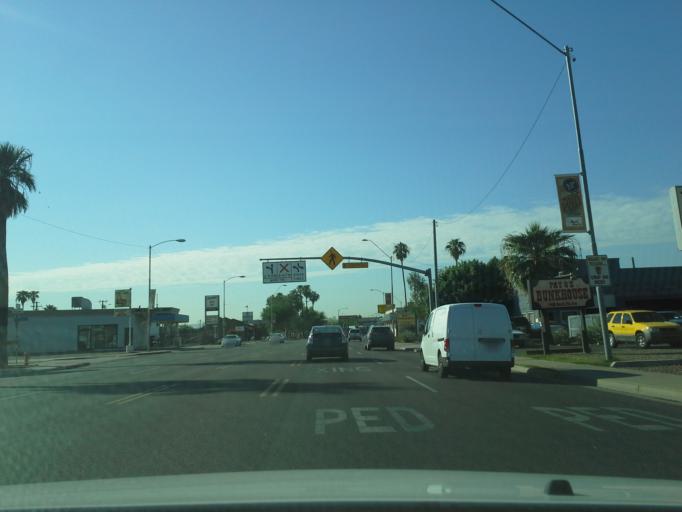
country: US
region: Arizona
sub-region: Maricopa County
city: Phoenix
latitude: 33.5015
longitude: -112.0825
